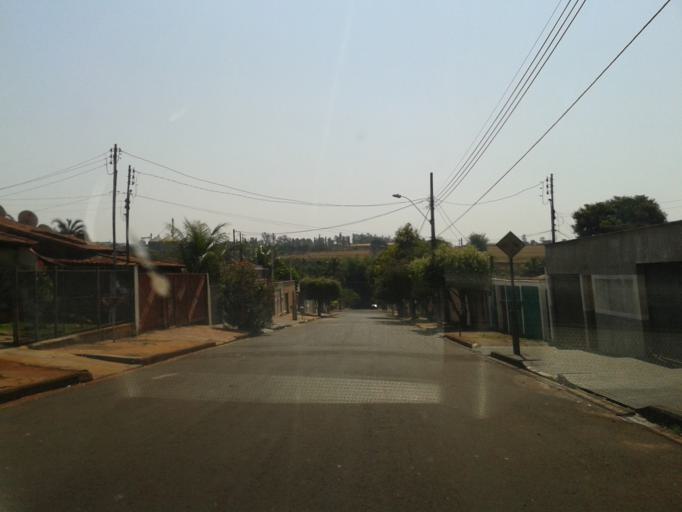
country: BR
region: Minas Gerais
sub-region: Ituiutaba
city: Ituiutaba
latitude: -18.9688
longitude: -49.4834
